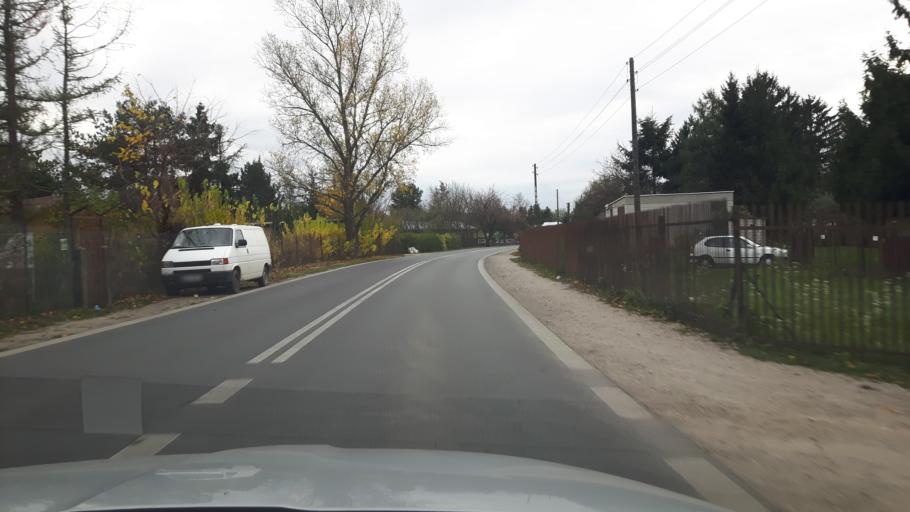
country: PL
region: Masovian Voivodeship
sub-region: Powiat wolominski
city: Zabki
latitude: 52.2805
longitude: 21.0961
